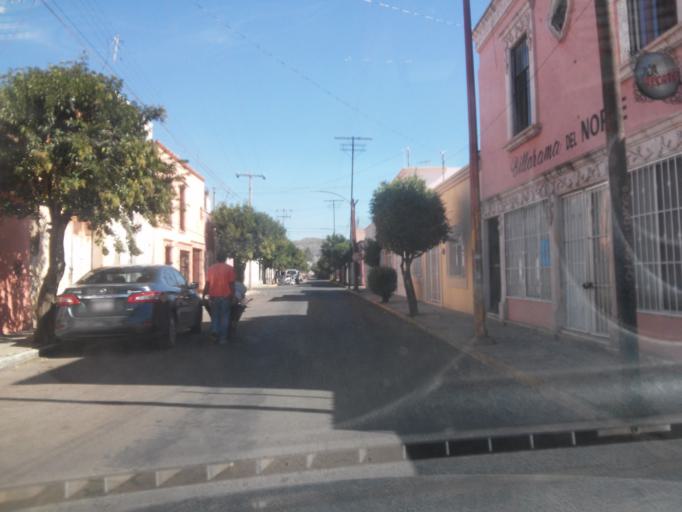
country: MX
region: Durango
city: Victoria de Durango
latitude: 24.0310
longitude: -104.6694
